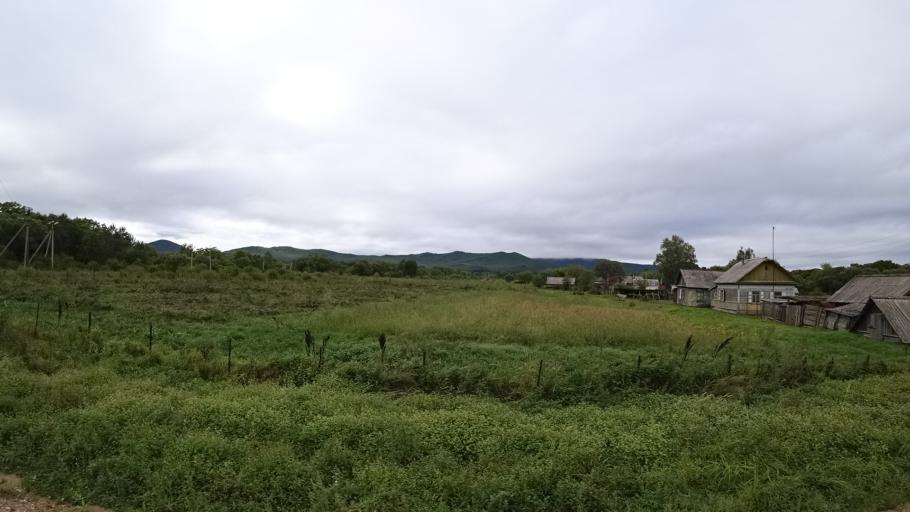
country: RU
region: Primorskiy
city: Rettikhovka
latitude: 44.1313
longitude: 132.6445
